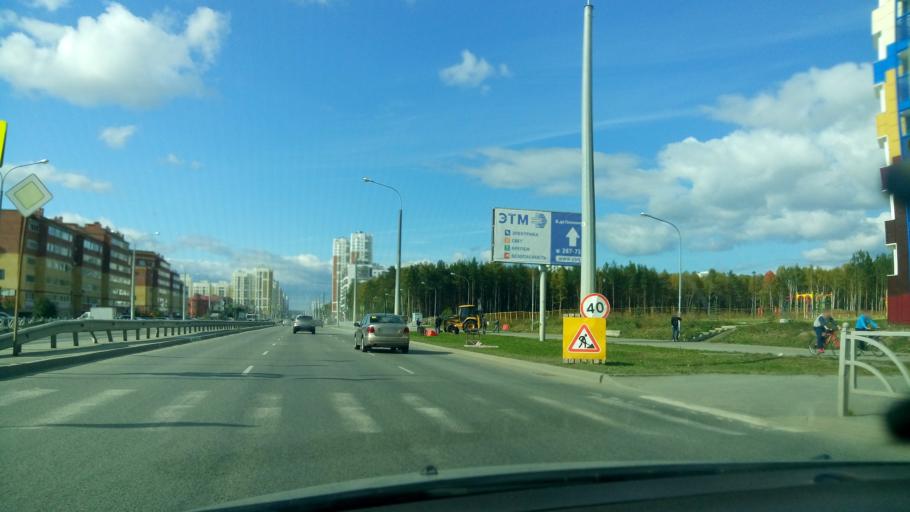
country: RU
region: Sverdlovsk
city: Sovkhoznyy
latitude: 56.7832
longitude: 60.5395
